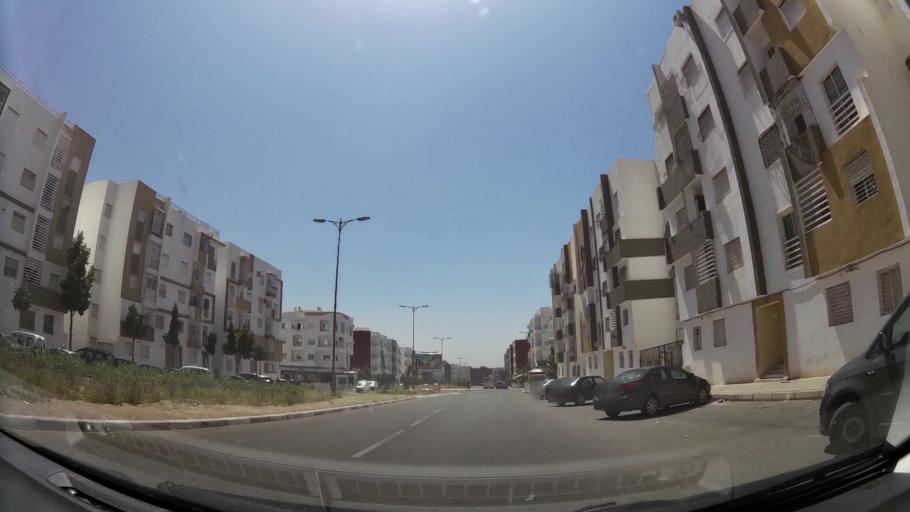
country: MA
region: Oued ed Dahab-Lagouira
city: Dakhla
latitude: 30.4330
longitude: -9.5569
